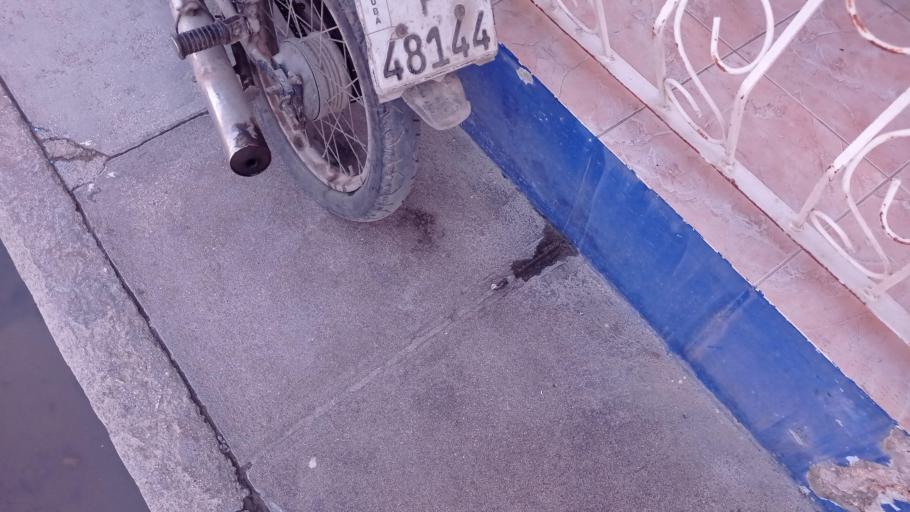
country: CU
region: Matanzas
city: Cardenas
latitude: 23.0444
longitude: -81.2136
